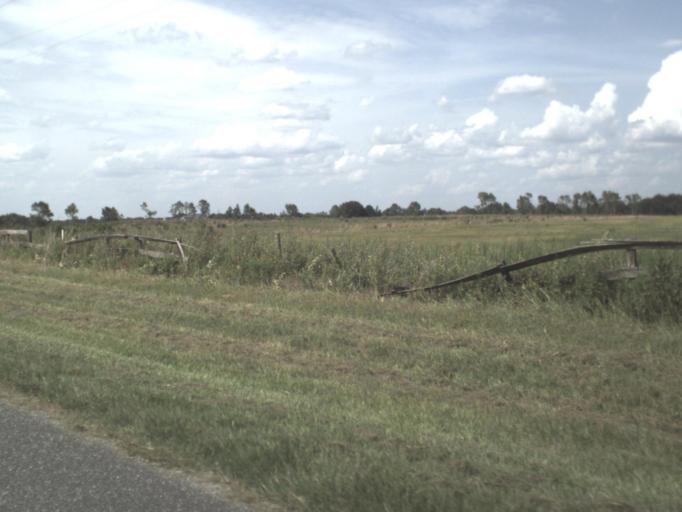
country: US
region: Florida
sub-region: Columbia County
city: Lake City
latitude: 30.0112
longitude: -82.7102
